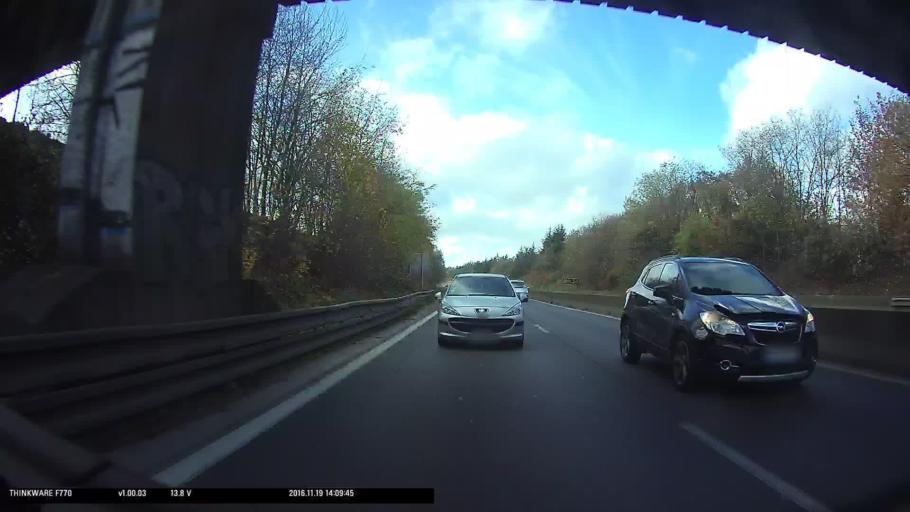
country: FR
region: Ile-de-France
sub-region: Departement du Val-d'Oise
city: Osny
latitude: 49.0527
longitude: 2.0629
